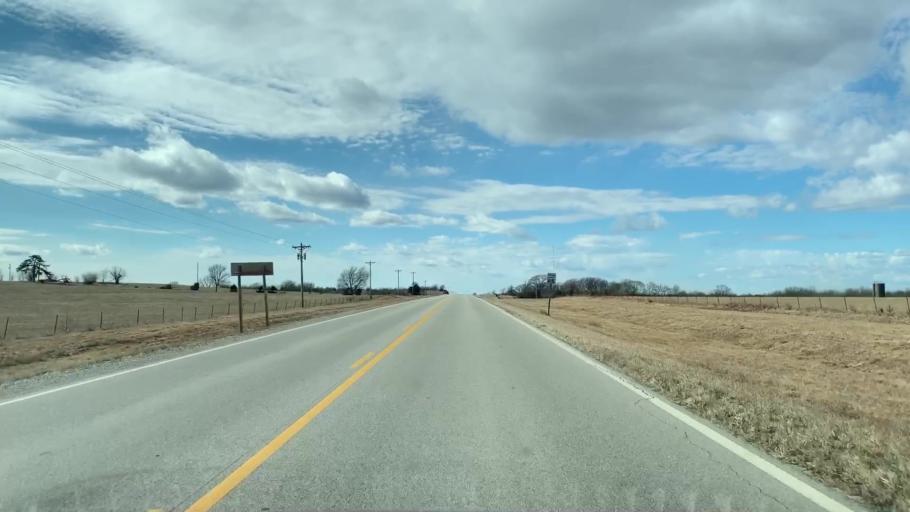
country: US
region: Kansas
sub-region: Neosho County
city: Erie
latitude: 37.5292
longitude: -95.3629
